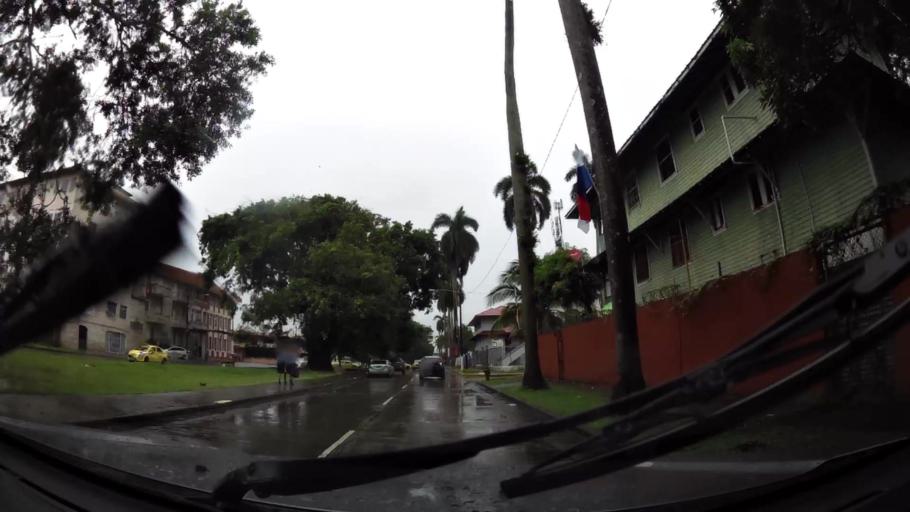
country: PA
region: Colon
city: Colon
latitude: 9.3612
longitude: -79.8975
